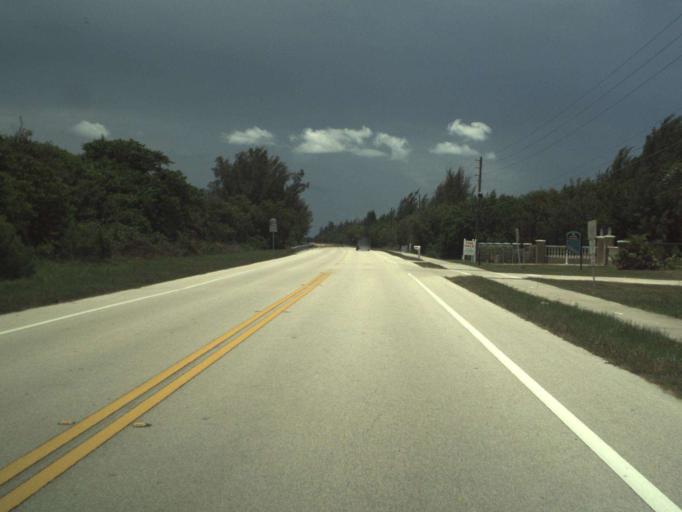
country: US
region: Florida
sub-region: Saint Lucie County
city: Indian River Estates
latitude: 27.3950
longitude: -80.2633
